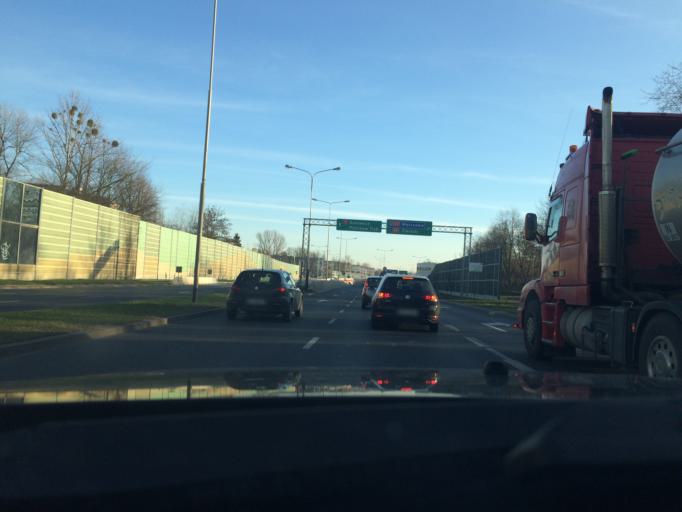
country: PL
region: Lodz Voivodeship
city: Lodz
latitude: 51.7296
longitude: 19.4436
